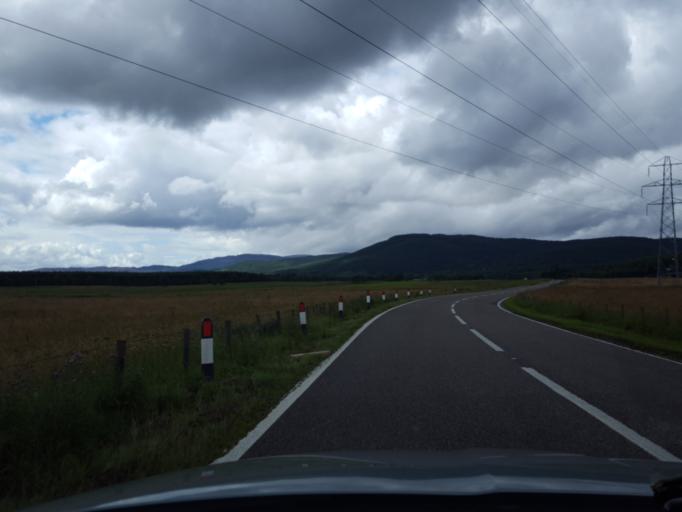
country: GB
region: Scotland
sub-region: Highland
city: Aviemore
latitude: 57.2560
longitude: -3.7632
